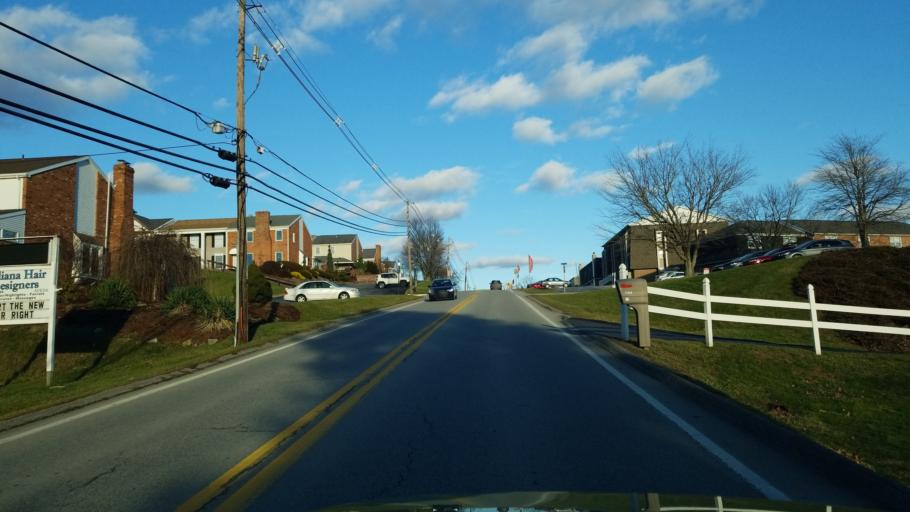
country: US
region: Pennsylvania
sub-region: Indiana County
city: Indiana
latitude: 40.6119
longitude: -79.1826
